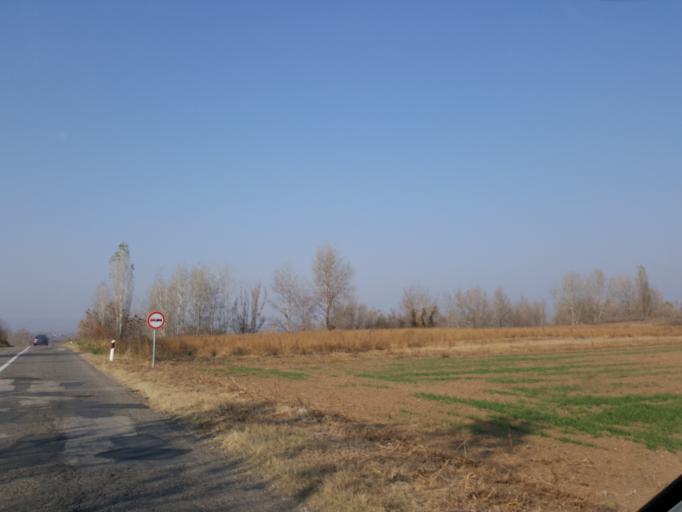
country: RS
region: Central Serbia
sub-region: Borski Okrug
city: Negotin
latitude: 44.2181
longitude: 22.5704
